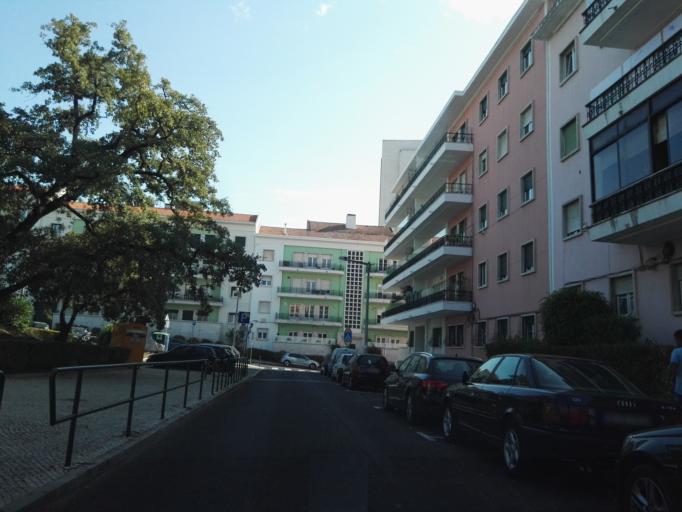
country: PT
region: Lisbon
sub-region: Lisbon
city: Lisbon
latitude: 38.7465
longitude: -9.1455
